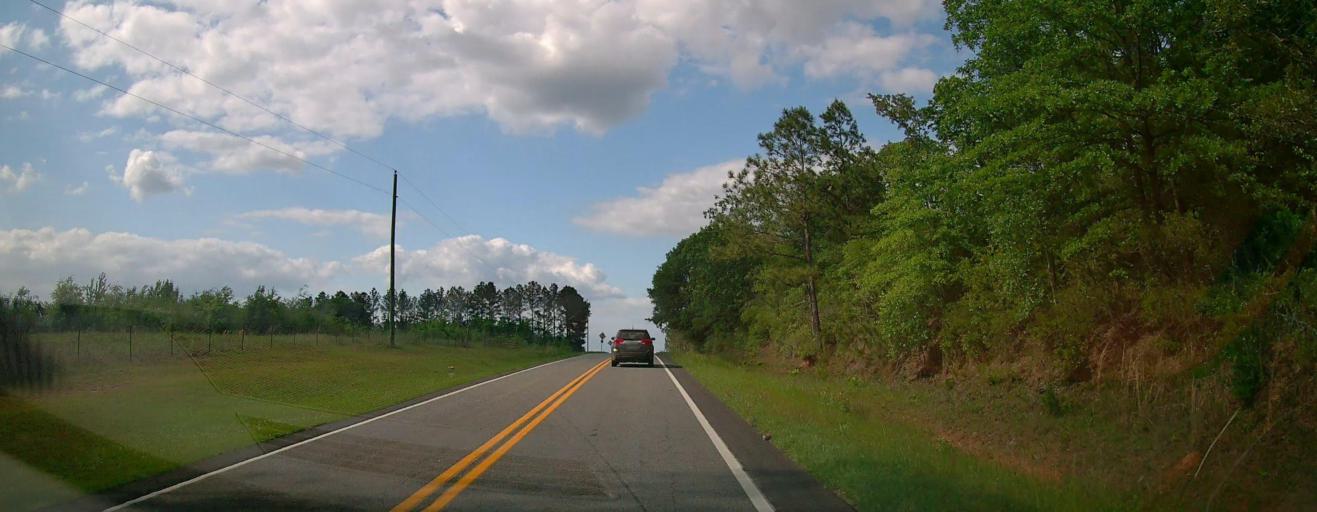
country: US
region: Georgia
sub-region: Laurens County
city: East Dublin
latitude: 32.6340
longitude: -82.8940
